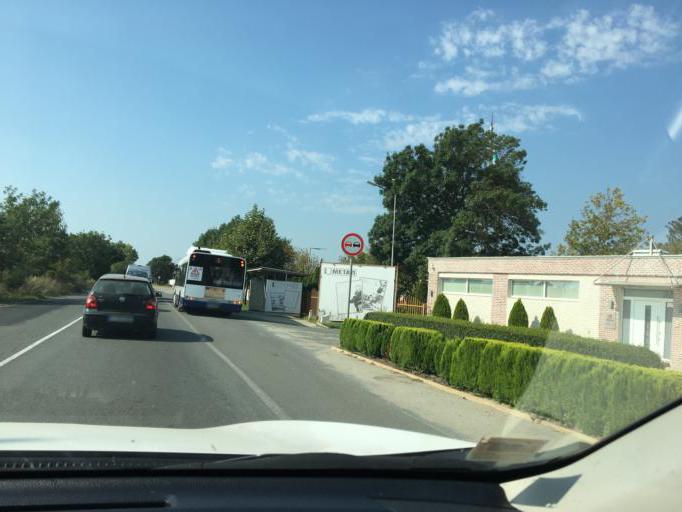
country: BG
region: Burgas
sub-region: Obshtina Burgas
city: Burgas
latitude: 42.5627
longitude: 27.4942
